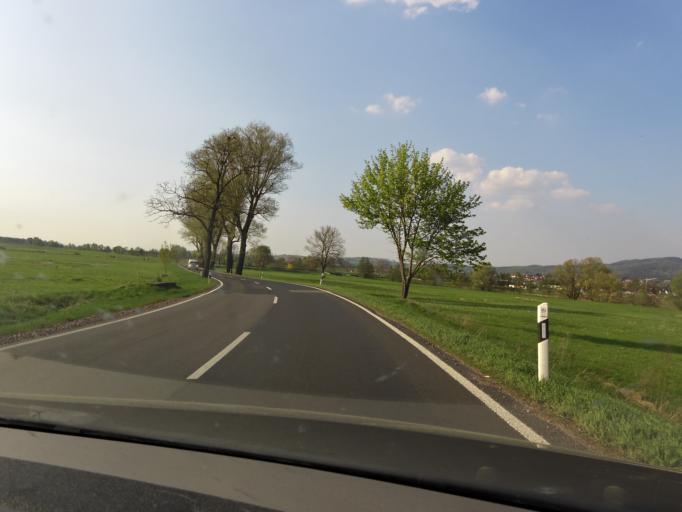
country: DE
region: Thuringia
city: Barchfeld
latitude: 50.8265
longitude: 10.2847
